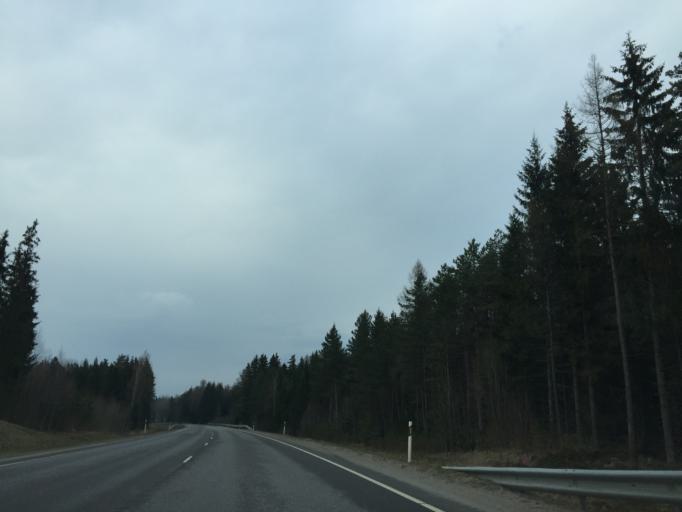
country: EE
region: Tartu
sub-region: UElenurme vald
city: Ulenurme
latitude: 58.0997
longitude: 26.7402
